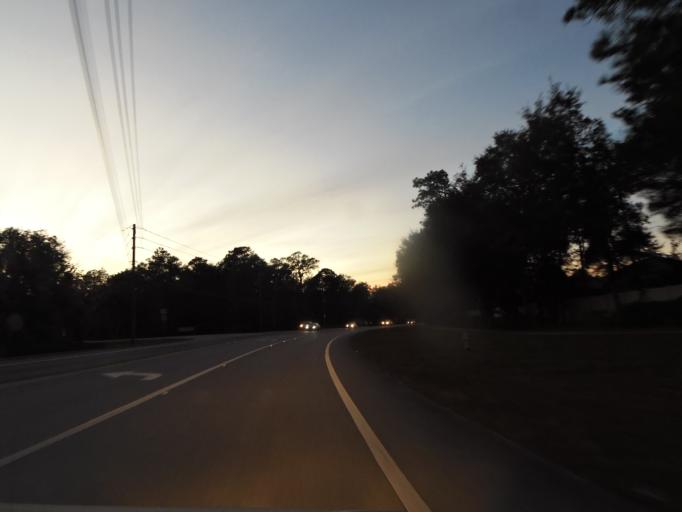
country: US
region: Florida
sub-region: Saint Johns County
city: Saint Augustine Shores
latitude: 29.8148
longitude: -81.3412
